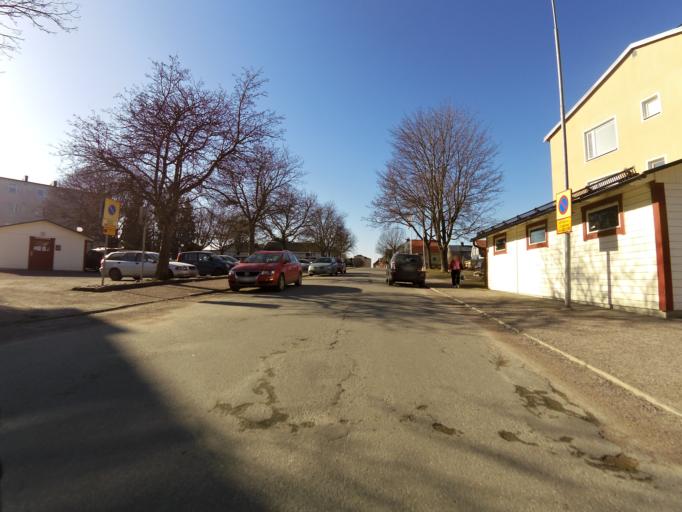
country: SE
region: Gaevleborg
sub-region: Gavle Kommun
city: Gavle
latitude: 60.6739
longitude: 17.1782
